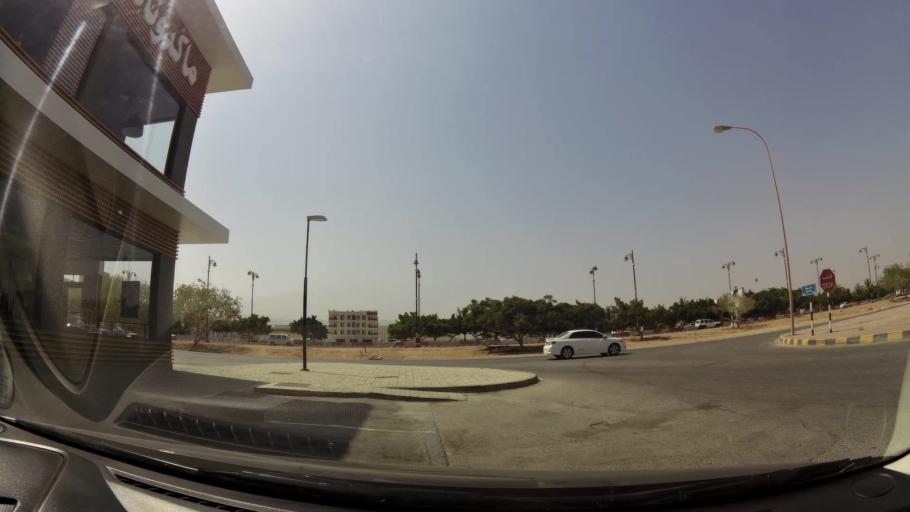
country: OM
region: Zufar
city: Salalah
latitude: 17.0215
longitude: 54.0684
